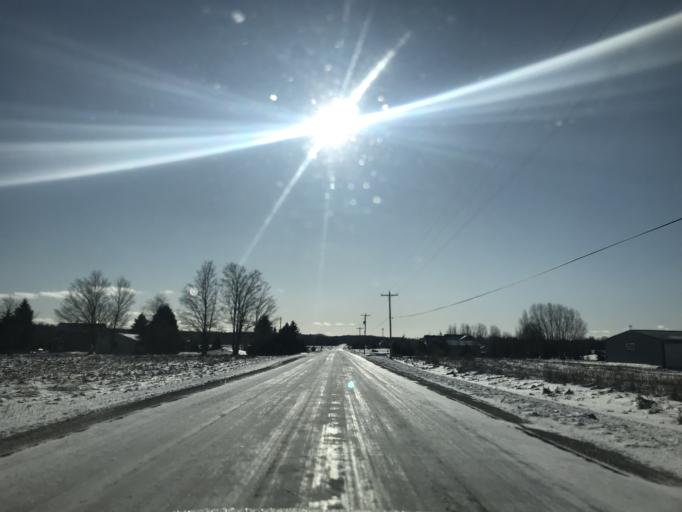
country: US
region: Wisconsin
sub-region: Door County
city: Sturgeon Bay
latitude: 44.8392
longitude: -87.5040
